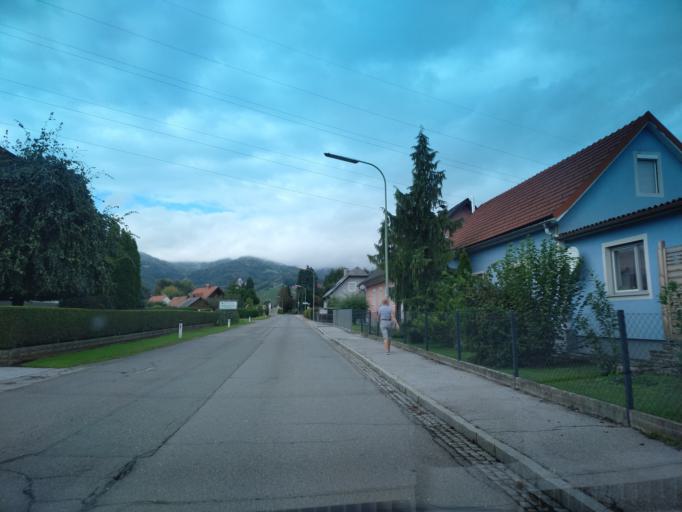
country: AT
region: Styria
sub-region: Politischer Bezirk Deutschlandsberg
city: Deutschlandsberg
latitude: 46.8158
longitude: 15.2292
